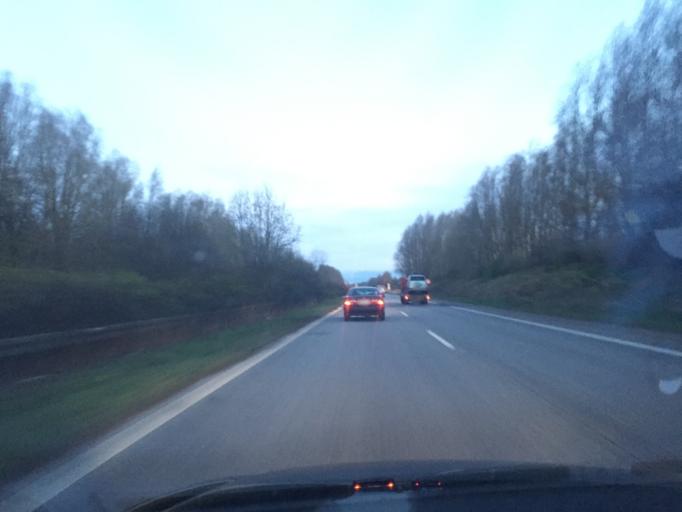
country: DK
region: Capital Region
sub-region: Fredensborg Kommune
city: Niva
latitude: 55.9457
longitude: 12.4782
